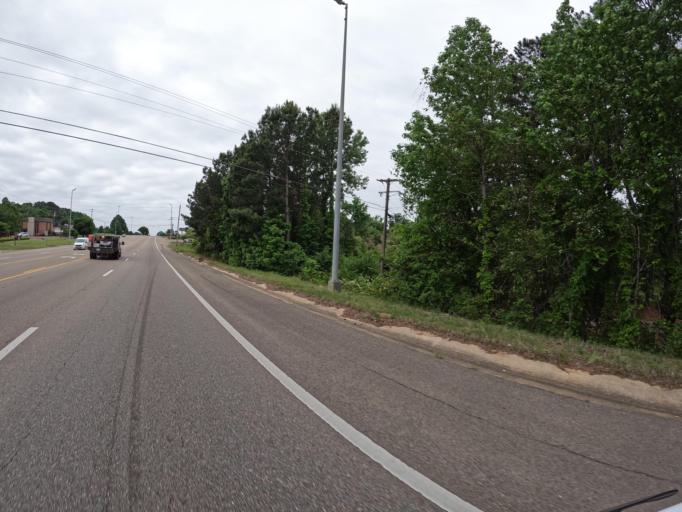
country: US
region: Mississippi
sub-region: Lee County
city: Tupelo
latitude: 34.2787
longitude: -88.7157
